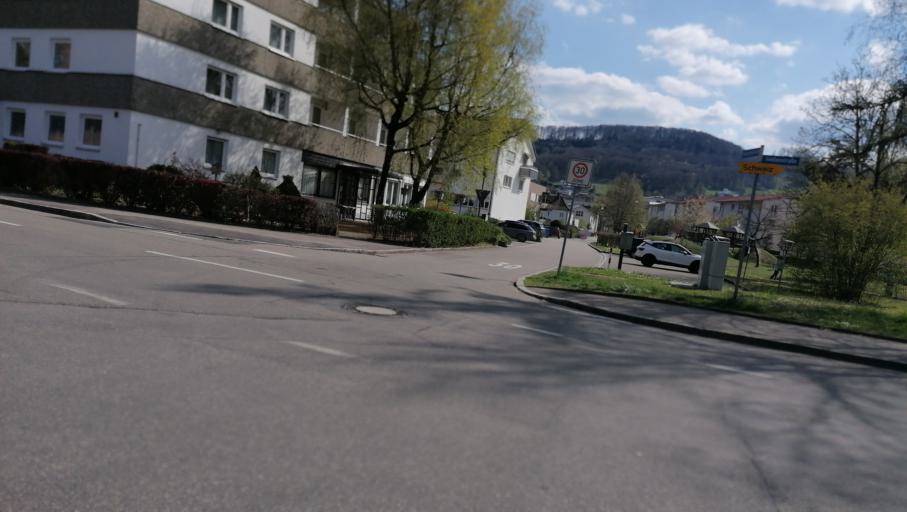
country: DE
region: Baden-Wuerttemberg
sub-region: Freiburg Region
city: Bad Sackingen
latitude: 47.5509
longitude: 7.9453
